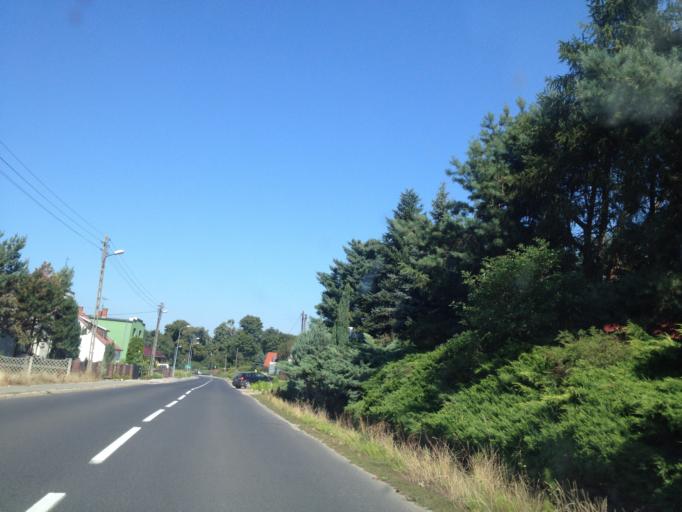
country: PL
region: Greater Poland Voivodeship
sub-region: Powiat poznanski
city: Kornik
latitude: 52.2323
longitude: 17.0998
